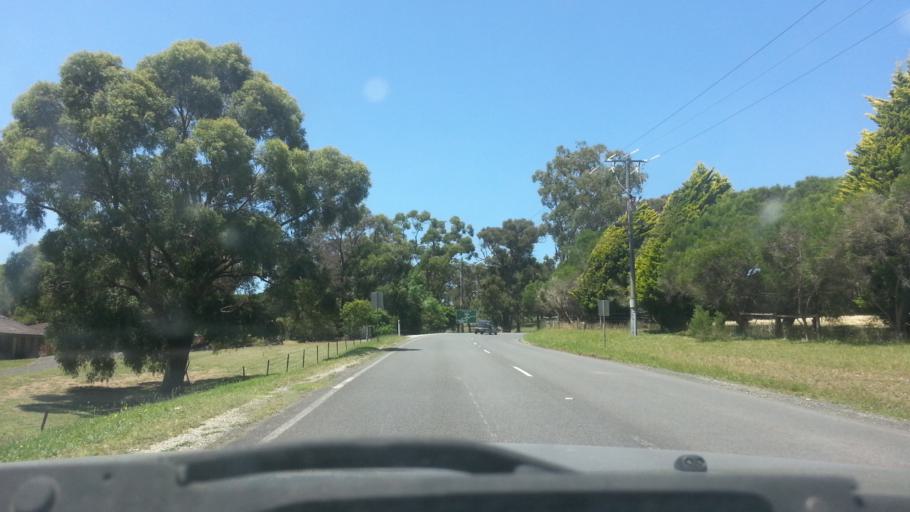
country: AU
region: Victoria
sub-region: Cardinia
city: Beaconsfield Upper
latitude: -37.9803
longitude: 145.3965
